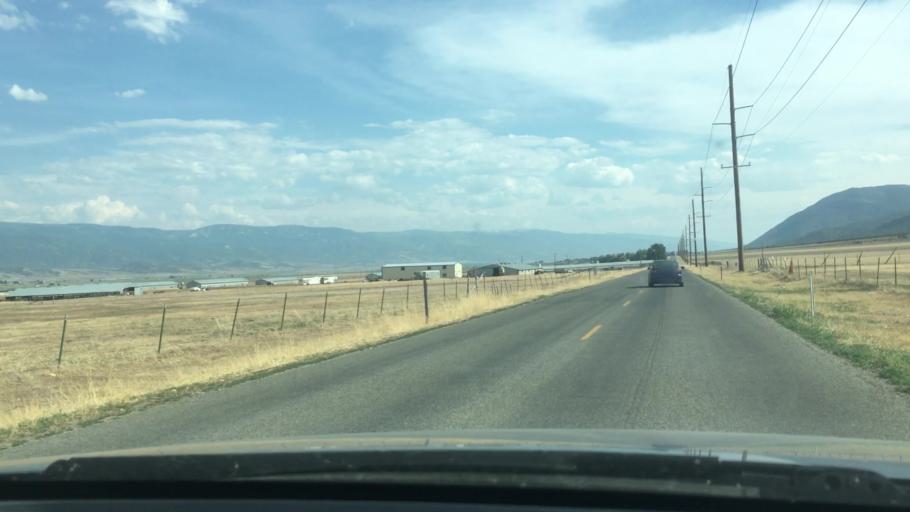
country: US
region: Utah
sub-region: Sanpete County
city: Moroni
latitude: 39.5334
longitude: -111.6398
